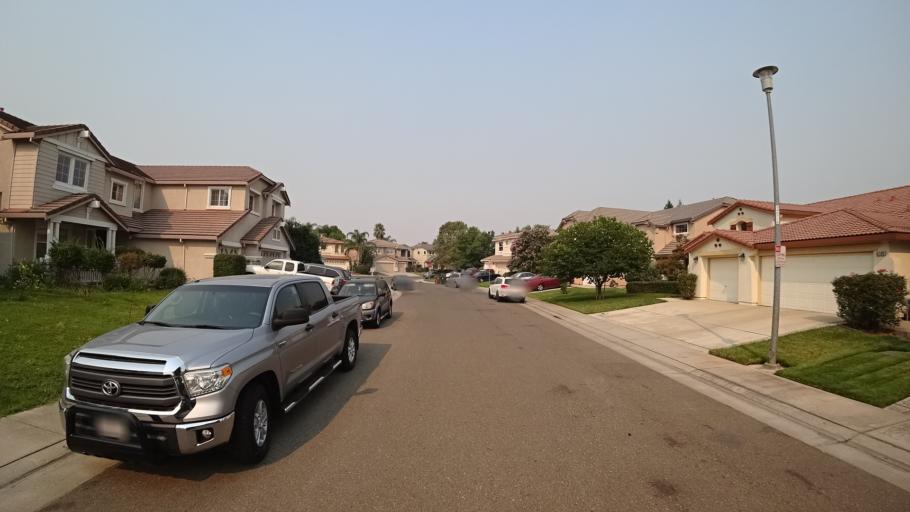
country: US
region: California
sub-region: Sacramento County
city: Laguna
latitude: 38.3964
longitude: -121.4316
